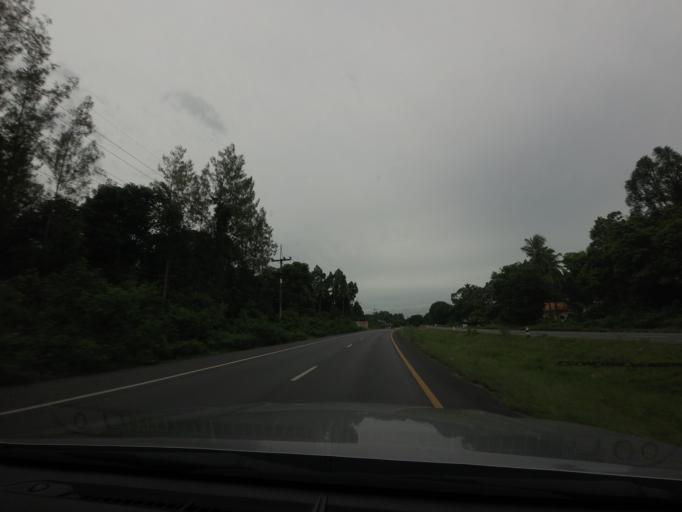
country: TH
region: Nakhon Si Thammarat
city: Chaloem Phra Kiat
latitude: 8.2251
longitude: 100.0223
